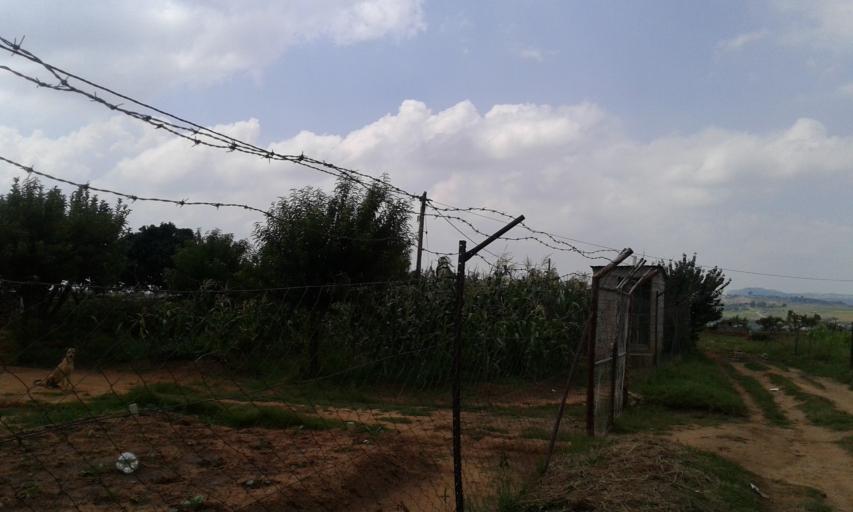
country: LS
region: Maseru
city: Maseru
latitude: -29.4315
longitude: 27.5742
